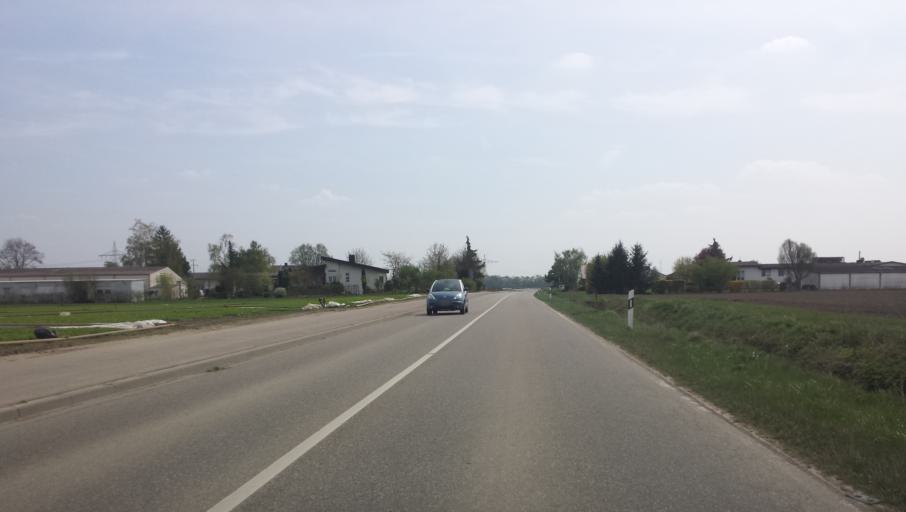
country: DE
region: Rheinland-Pfalz
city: Mutterstadt
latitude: 49.4594
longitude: 8.3368
